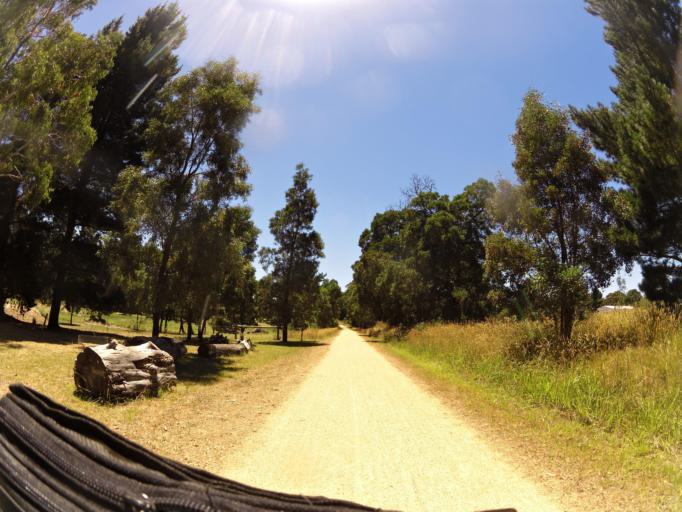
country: AU
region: Victoria
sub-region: Ballarat North
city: Delacombe
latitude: -37.6391
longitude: 143.6874
